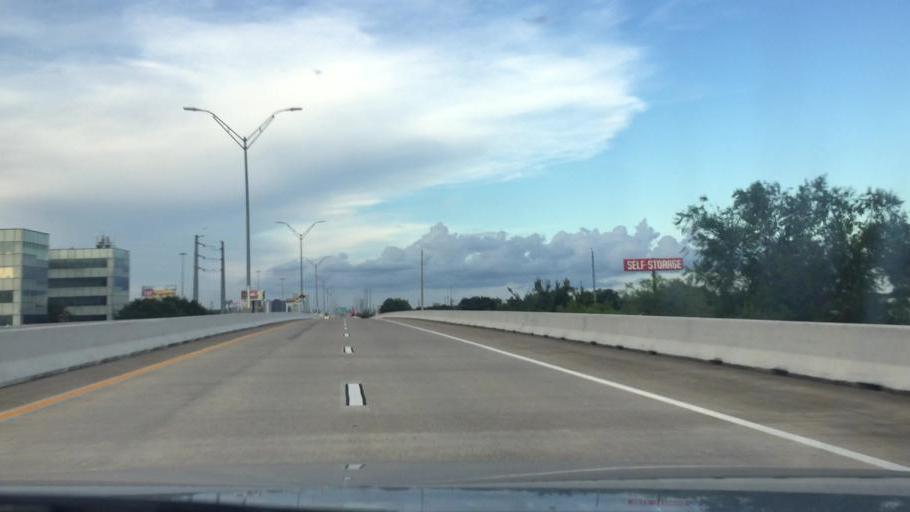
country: US
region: Texas
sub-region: Harris County
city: Bellaire
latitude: 29.7242
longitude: -95.4835
